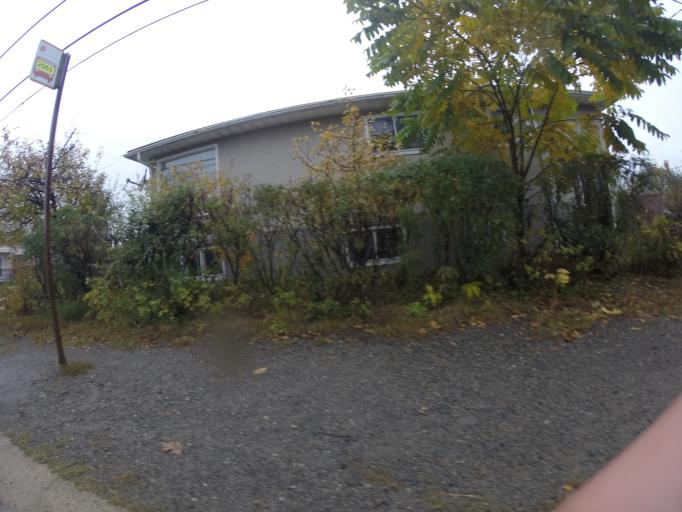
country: CA
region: Ontario
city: Greater Sudbury
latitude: 46.4743
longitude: -81.0297
